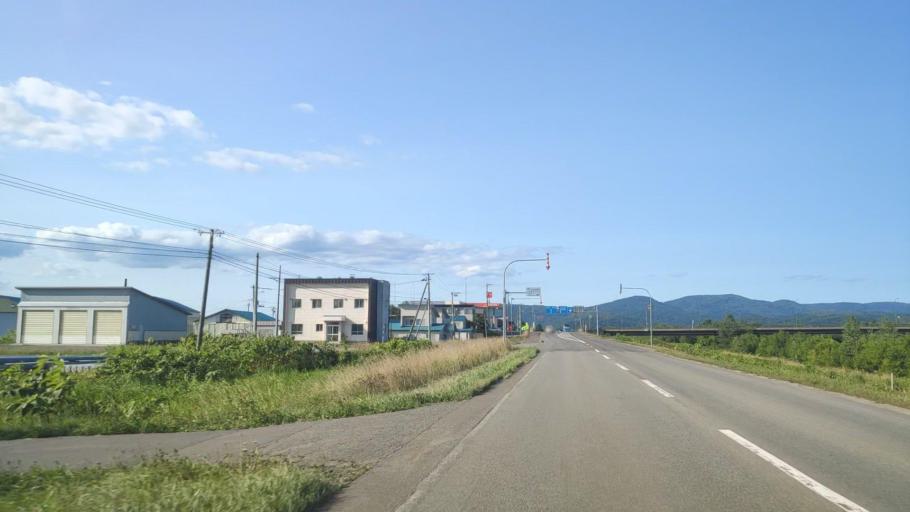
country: JP
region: Hokkaido
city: Makubetsu
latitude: 44.8164
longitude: 142.0669
